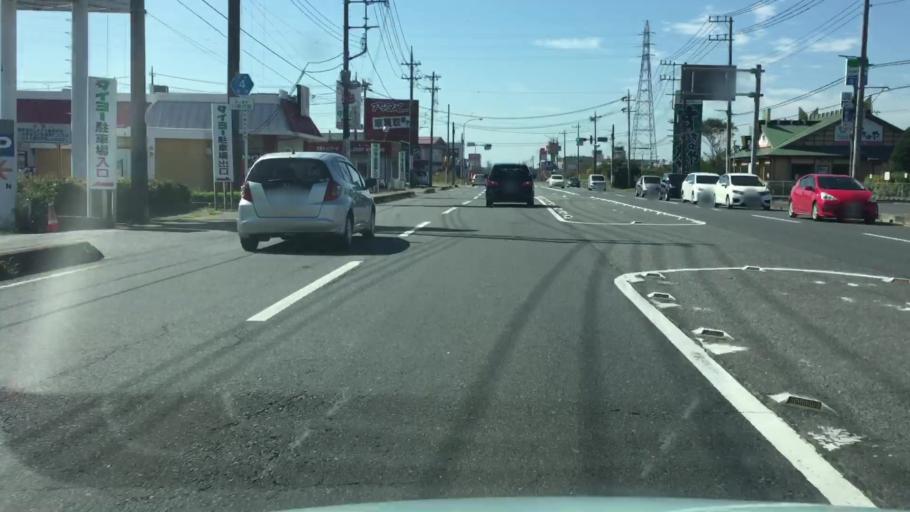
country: JP
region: Ibaraki
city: Ryugasaki
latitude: 35.9076
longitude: 140.1727
